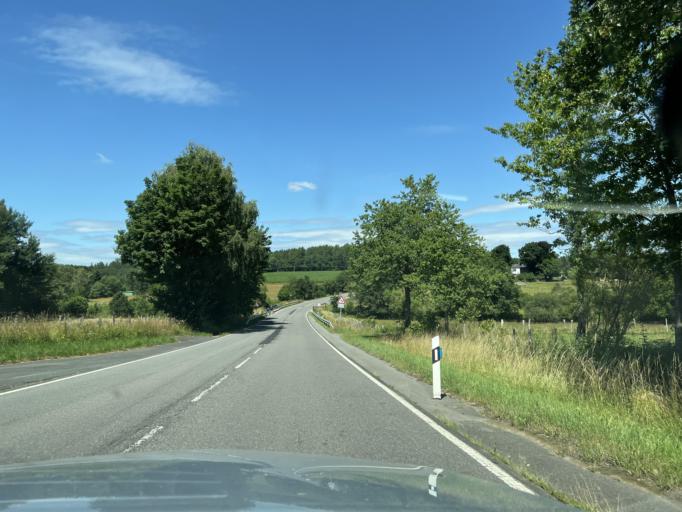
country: DE
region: North Rhine-Westphalia
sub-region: Regierungsbezirk Arnsberg
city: Wenden
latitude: 50.9448
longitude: 7.8858
